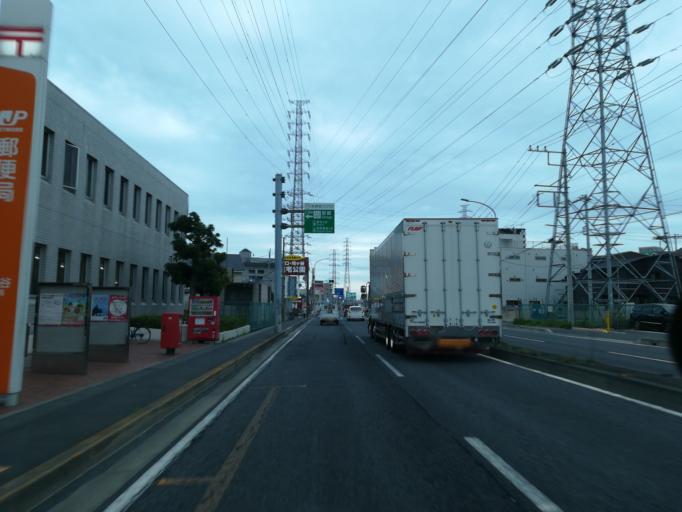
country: JP
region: Saitama
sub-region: Kawaguchi-shi
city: Hatogaya-honcho
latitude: 35.8337
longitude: 139.7348
